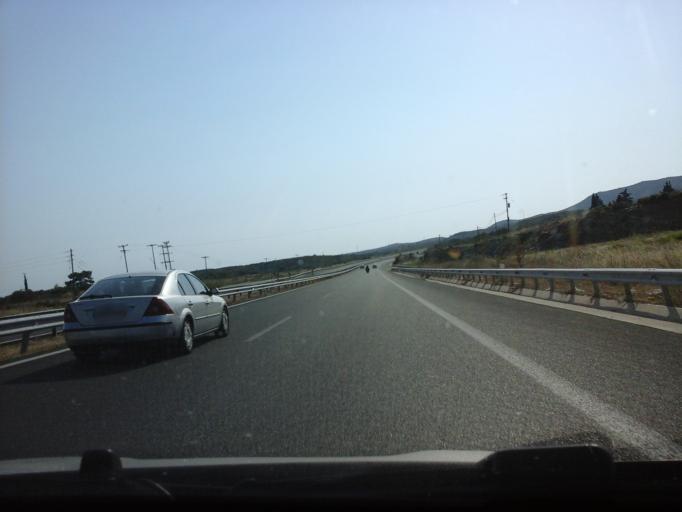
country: GR
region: East Macedonia and Thrace
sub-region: Nomos Evrou
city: Alexandroupoli
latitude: 40.8696
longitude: 25.7844
